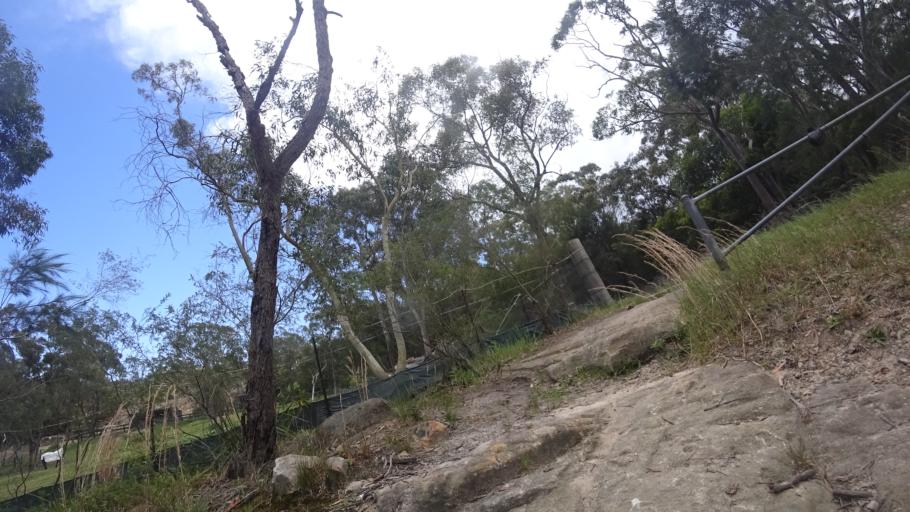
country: AU
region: New South Wales
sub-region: City of Sydney
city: North Turramurra
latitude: -33.6791
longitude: 151.1932
